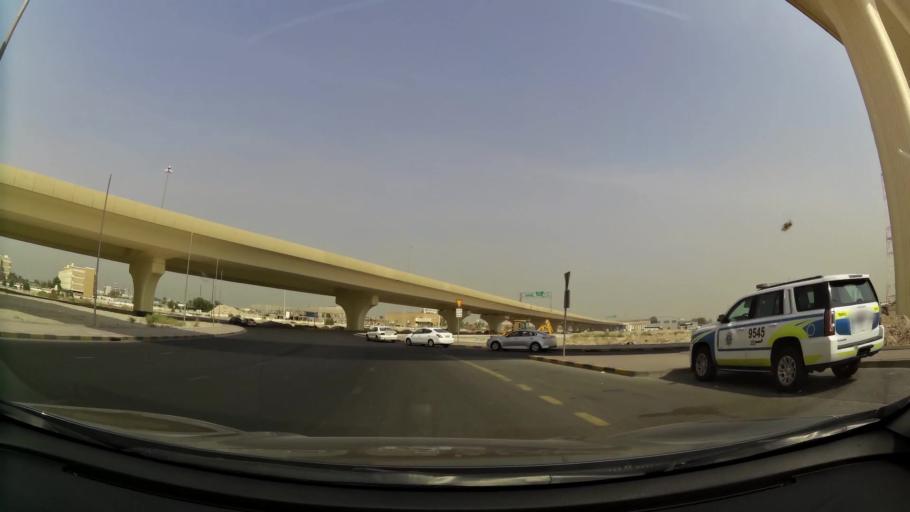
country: KW
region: Al Asimah
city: Ar Rabiyah
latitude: 29.3102
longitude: 47.8870
